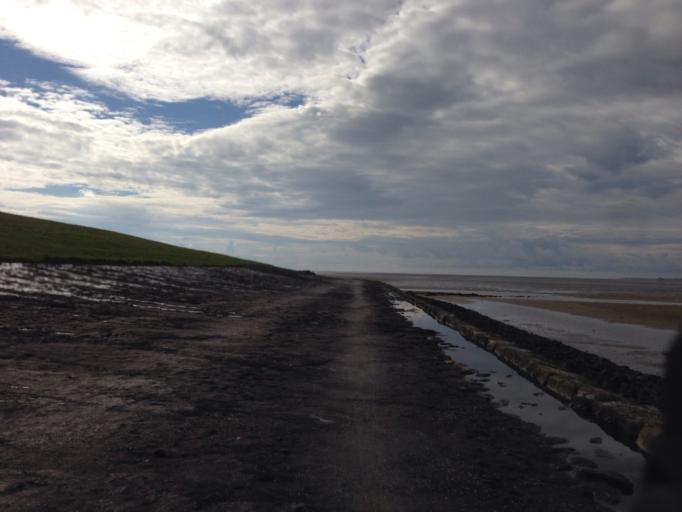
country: DE
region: Schleswig-Holstein
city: Dunsum
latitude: 54.7429
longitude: 8.4220
